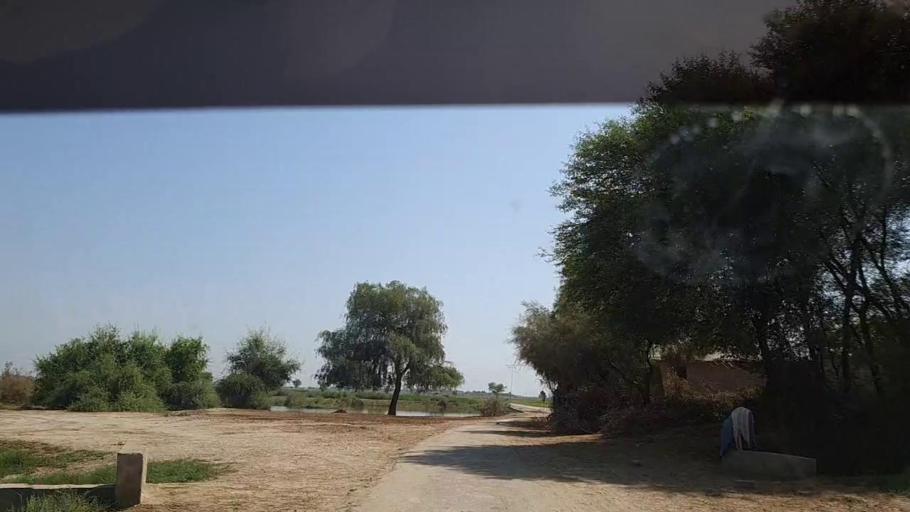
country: PK
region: Sindh
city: Kandhkot
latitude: 28.1825
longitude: 69.1592
